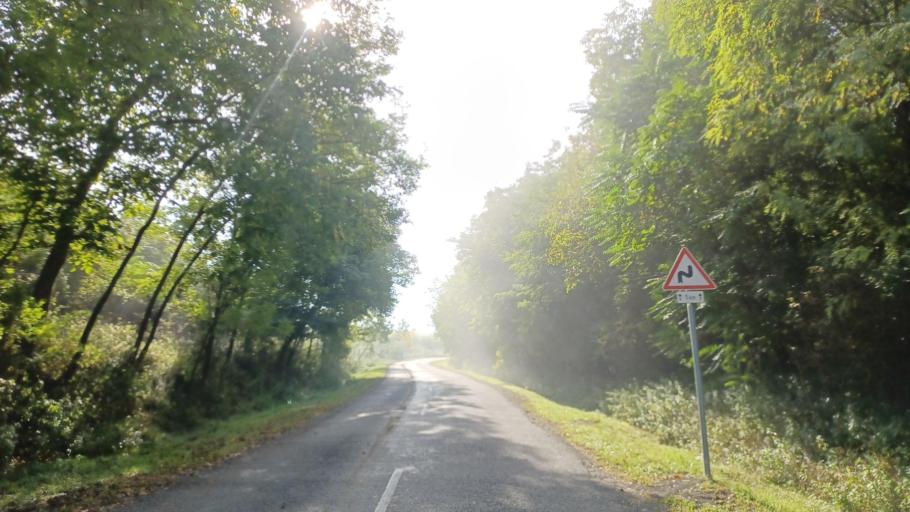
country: HU
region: Tolna
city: Pincehely
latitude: 46.6771
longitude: 18.4669
